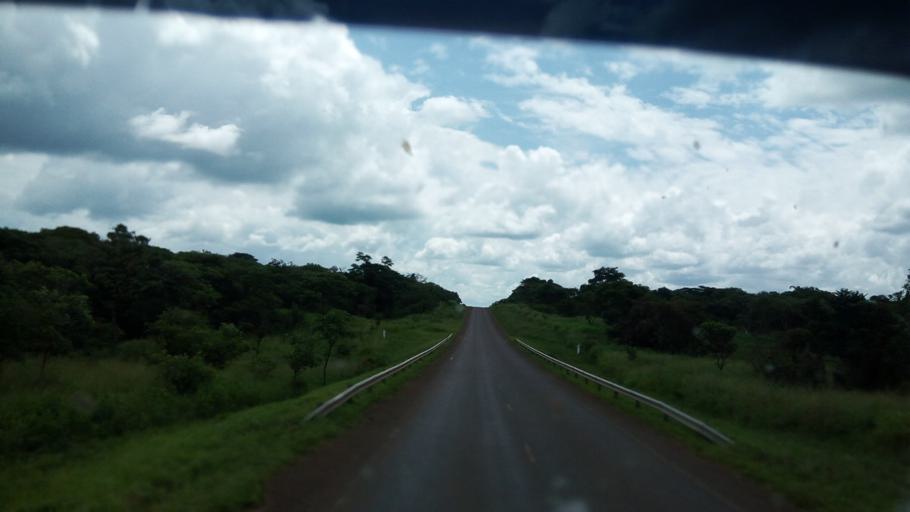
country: UG
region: Northern Region
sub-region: Oyam District
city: Oyam
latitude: 2.3022
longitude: 32.1852
